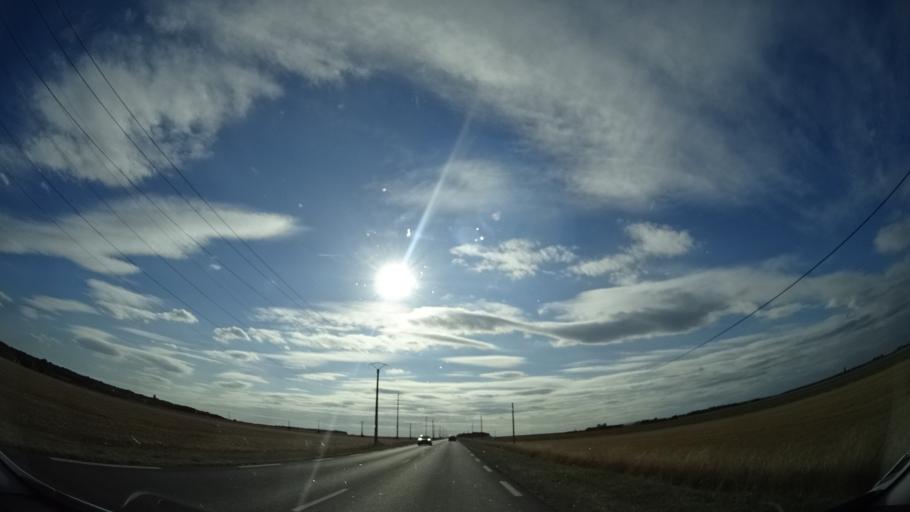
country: FR
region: Centre
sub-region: Departement du Loir-et-Cher
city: Moree
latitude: 47.9043
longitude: 1.2965
